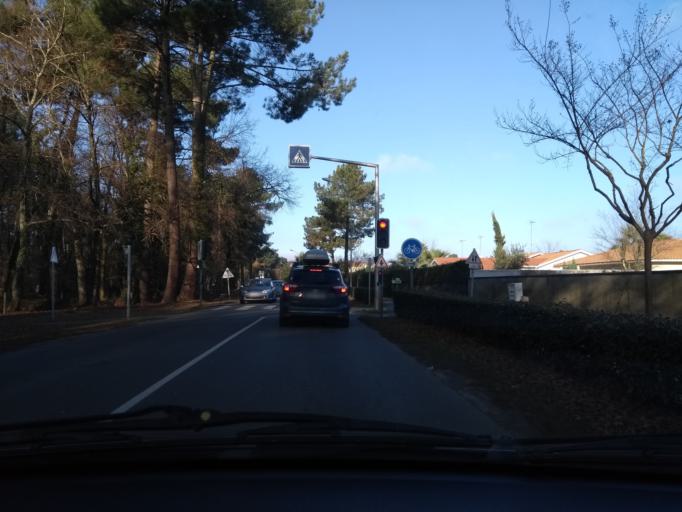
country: FR
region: Aquitaine
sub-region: Departement de la Gironde
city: Gujan-Mestras
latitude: 44.6202
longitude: -1.0732
